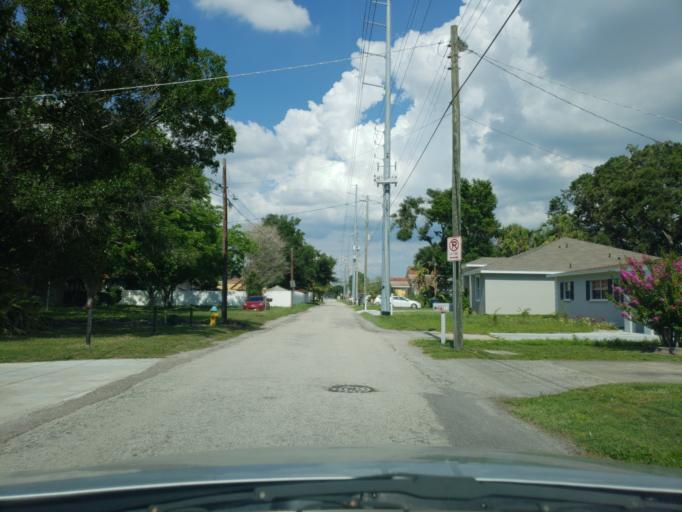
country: US
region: Florida
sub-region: Hillsborough County
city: Egypt Lake-Leto
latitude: 27.9762
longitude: -82.4947
